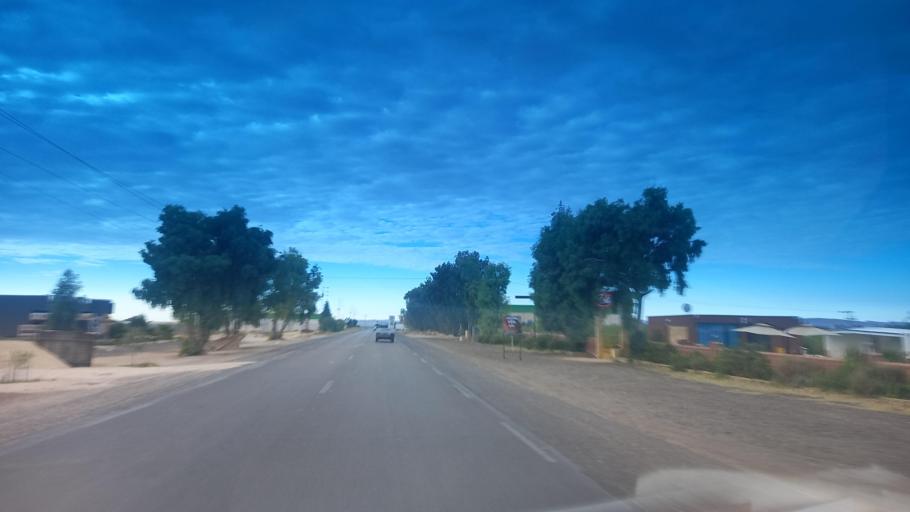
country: TN
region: Al Qasrayn
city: Sbiba
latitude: 35.2867
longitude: 9.0926
